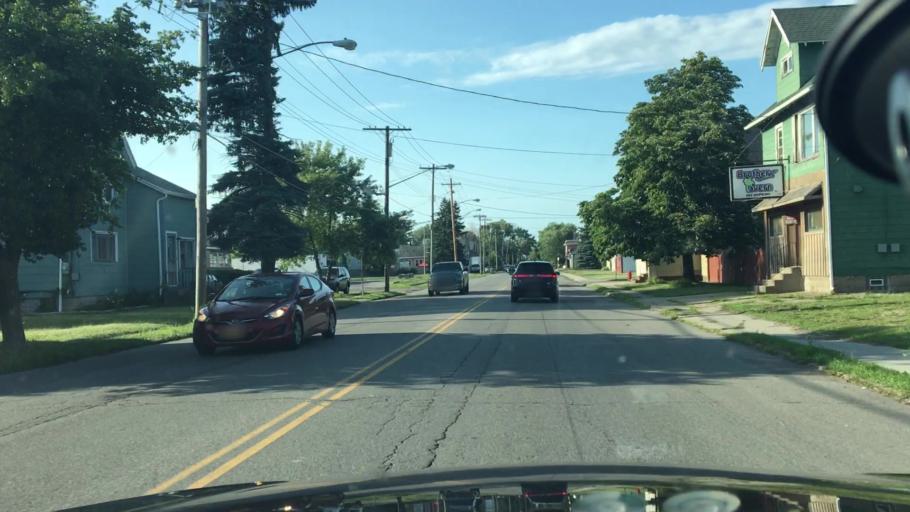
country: US
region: New York
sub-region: Erie County
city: Lackawanna
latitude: 42.8508
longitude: -78.8323
